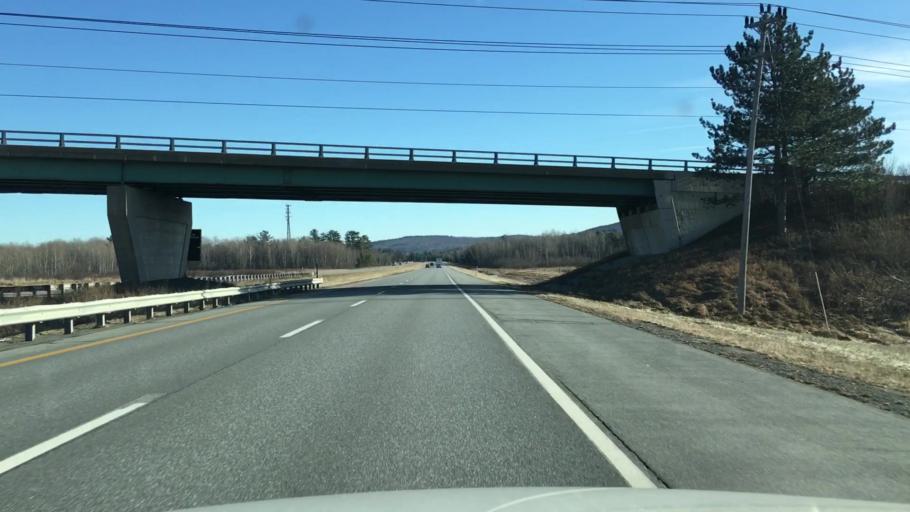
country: US
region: Maine
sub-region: Penobscot County
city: Brewer
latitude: 44.7740
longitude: -68.7465
